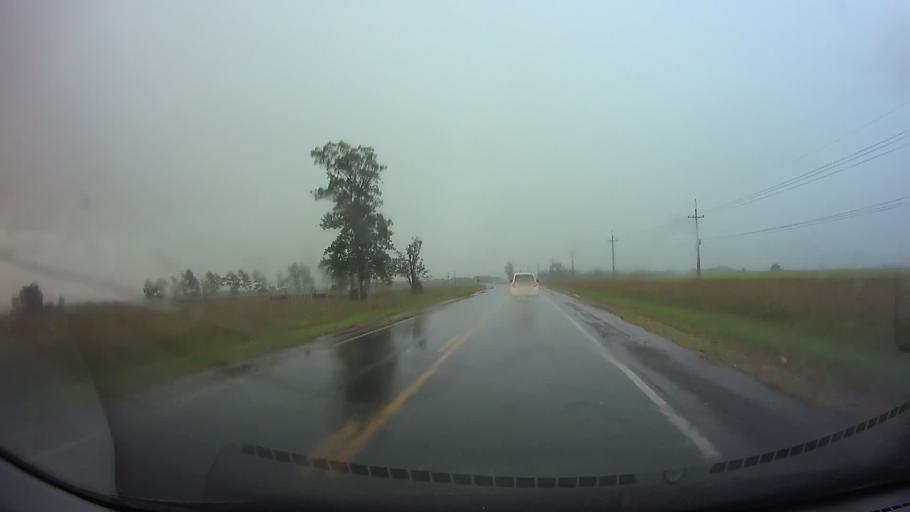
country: PY
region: Paraguari
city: Paraguari
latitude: -25.6551
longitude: -57.1604
